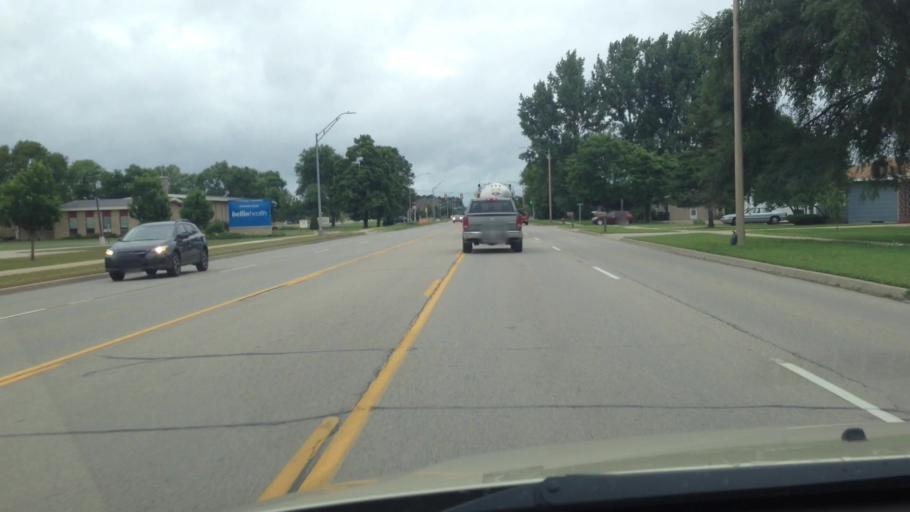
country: US
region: Michigan
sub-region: Delta County
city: Escanaba
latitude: 45.7373
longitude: -87.0799
